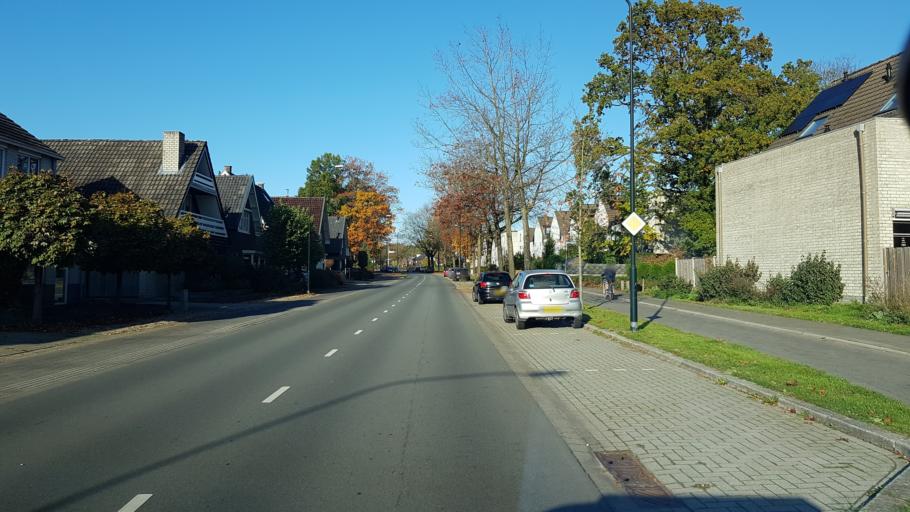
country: NL
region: Gelderland
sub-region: Gemeente Apeldoorn
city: Apeldoorn
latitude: 52.2033
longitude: 5.9445
